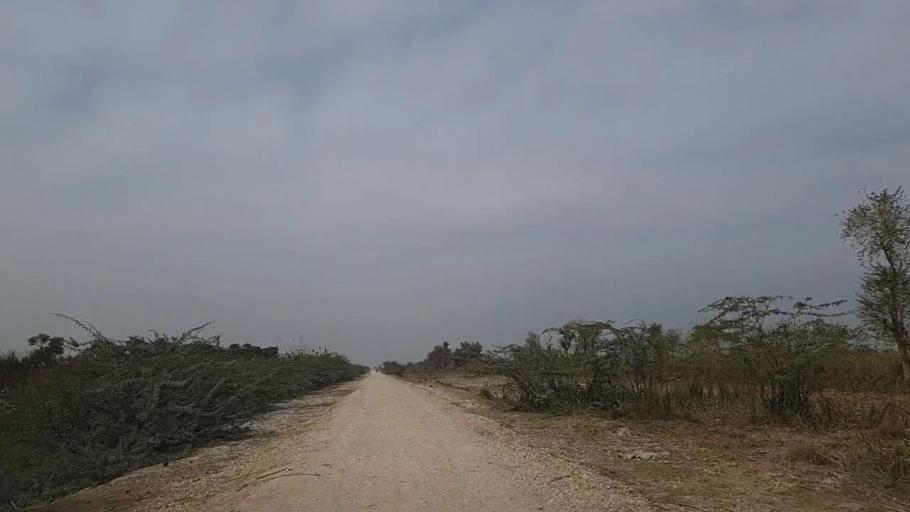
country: PK
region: Sindh
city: Daur
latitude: 26.4082
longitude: 68.4342
